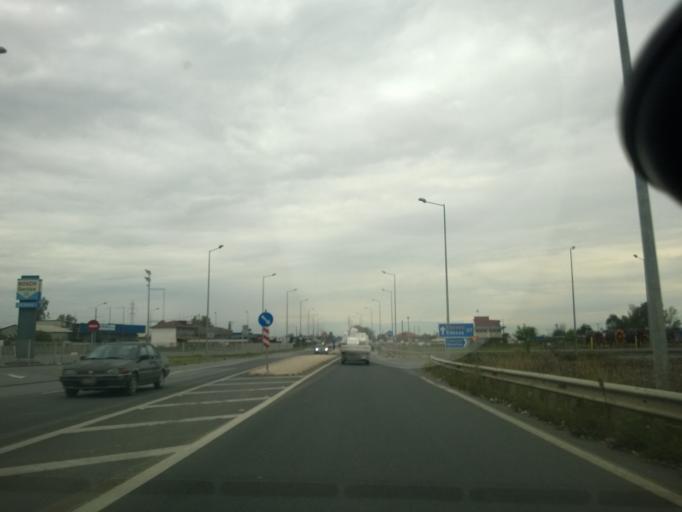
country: GR
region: Central Macedonia
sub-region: Nomos Pellis
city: Giannitsa
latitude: 40.7832
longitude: 22.3914
